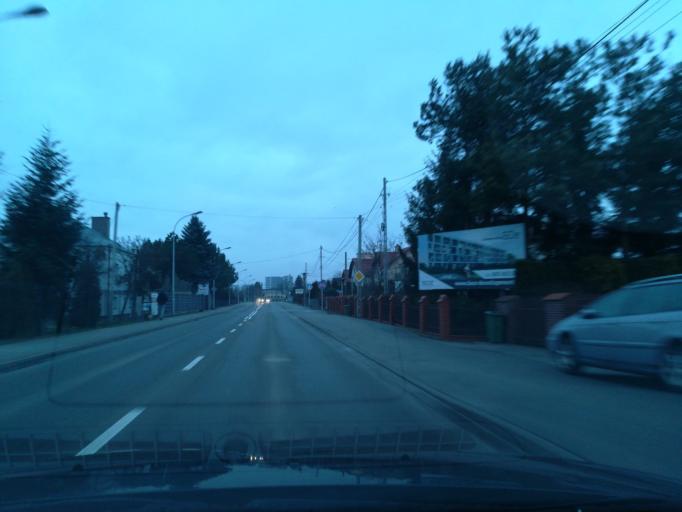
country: PL
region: Subcarpathian Voivodeship
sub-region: Rzeszow
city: Rzeszow
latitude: 50.0080
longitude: 22.0047
